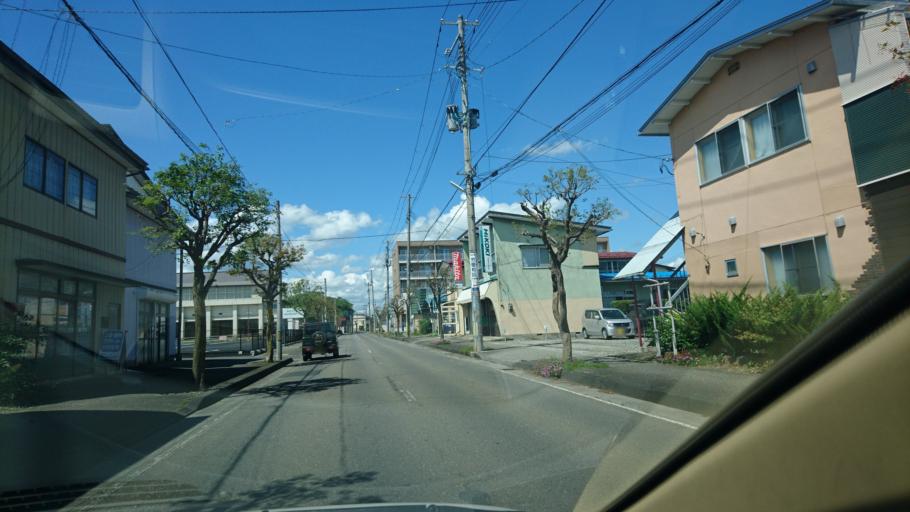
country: JP
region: Iwate
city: Kitakami
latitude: 39.2880
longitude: 141.1092
